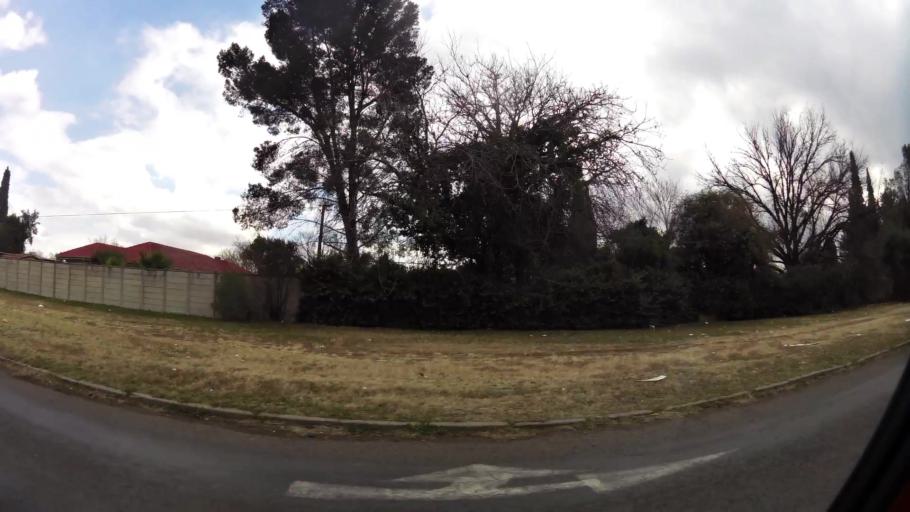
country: ZA
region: Gauteng
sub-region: Sedibeng District Municipality
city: Vanderbijlpark
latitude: -26.7077
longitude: 27.8359
